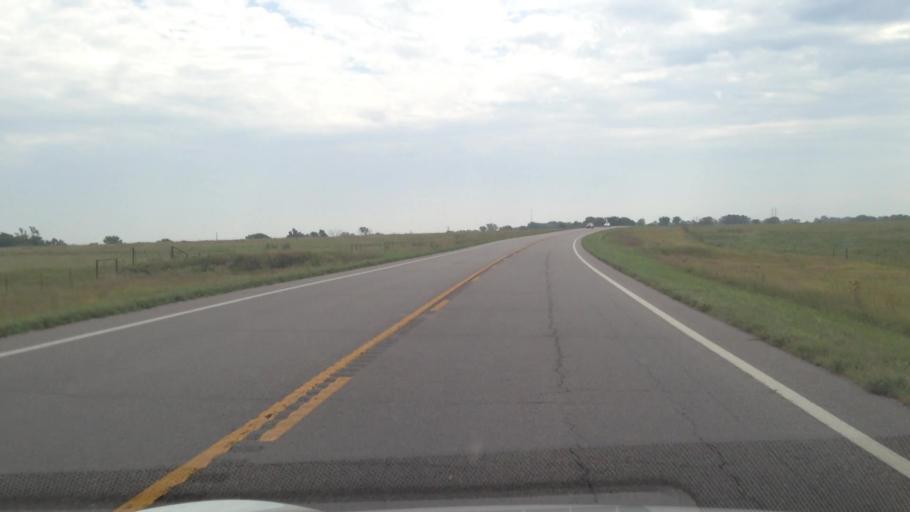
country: US
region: Kansas
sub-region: Bourbon County
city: Fort Scott
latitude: 37.8807
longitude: -95.0093
